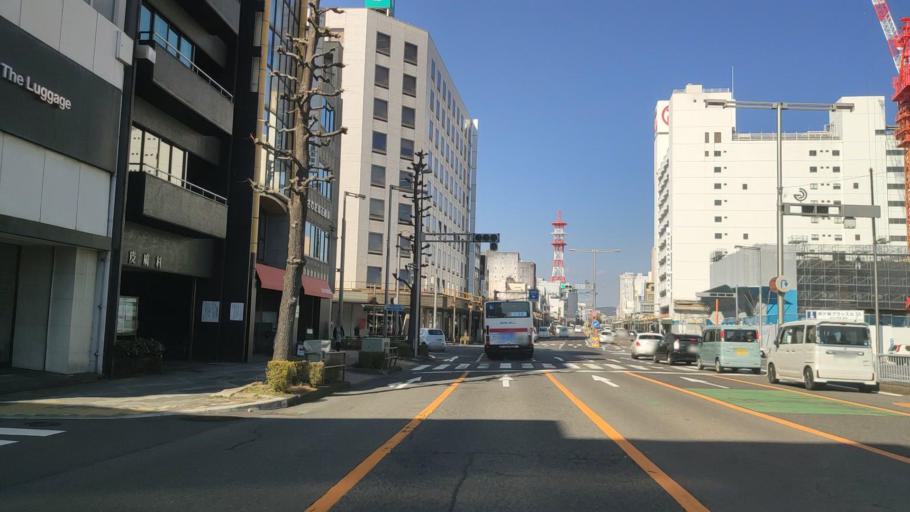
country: JP
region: Gifu
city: Gifu-shi
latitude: 35.4169
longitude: 136.7569
